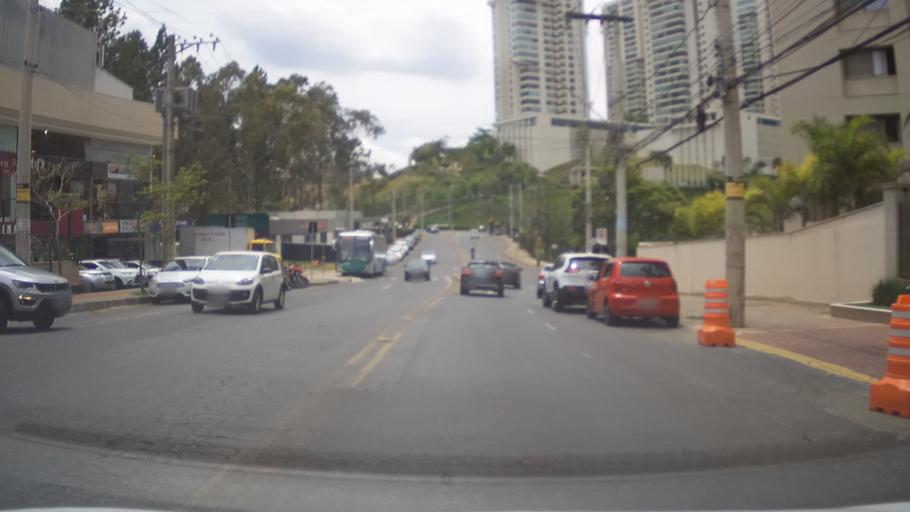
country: BR
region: Minas Gerais
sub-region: Belo Horizonte
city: Belo Horizonte
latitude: -19.9754
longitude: -43.9380
